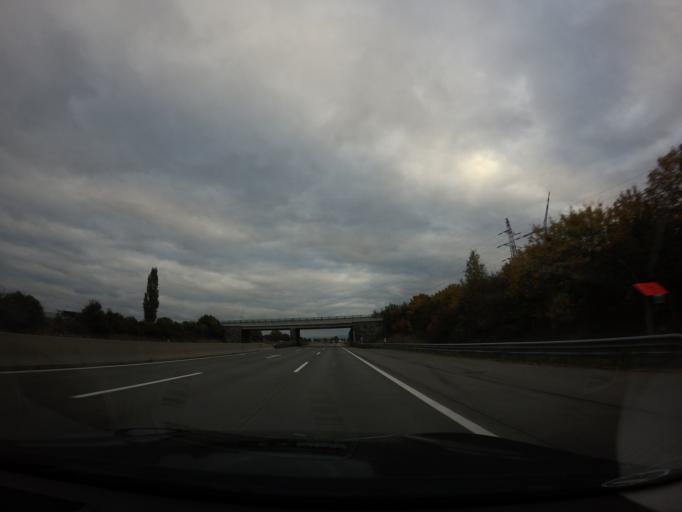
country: AT
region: Lower Austria
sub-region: Politischer Bezirk Sankt Polten
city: Haunoldstein
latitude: 48.1815
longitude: 15.4483
